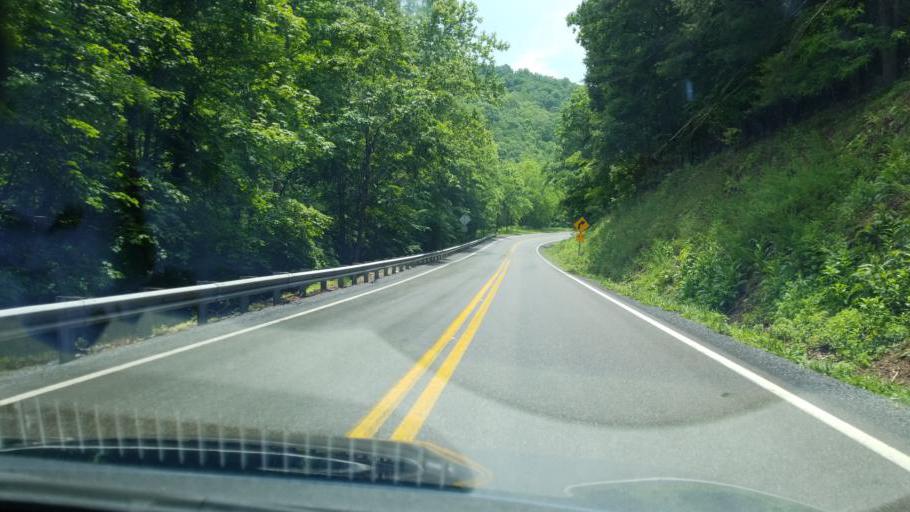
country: US
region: West Virginia
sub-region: Pendleton County
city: Franklin
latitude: 38.6540
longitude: -79.3486
